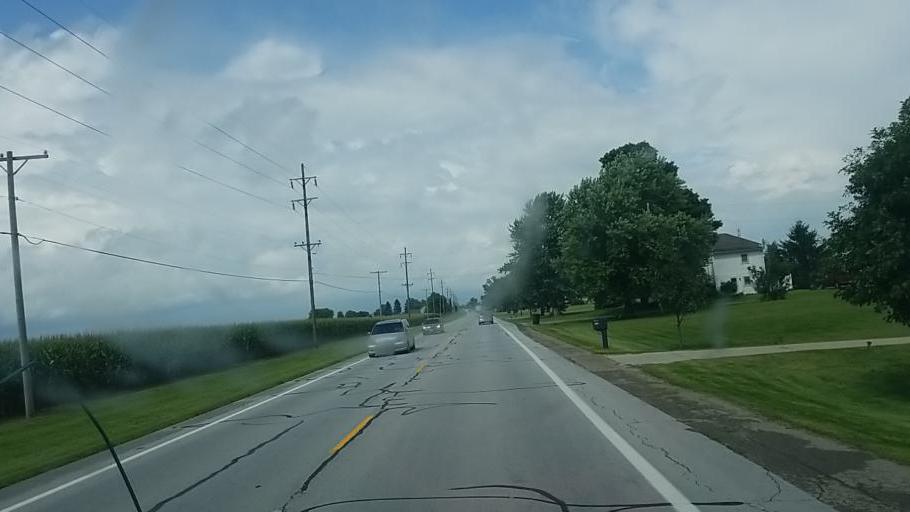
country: US
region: Ohio
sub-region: Logan County
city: West Liberty
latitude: 40.1813
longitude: -83.7429
